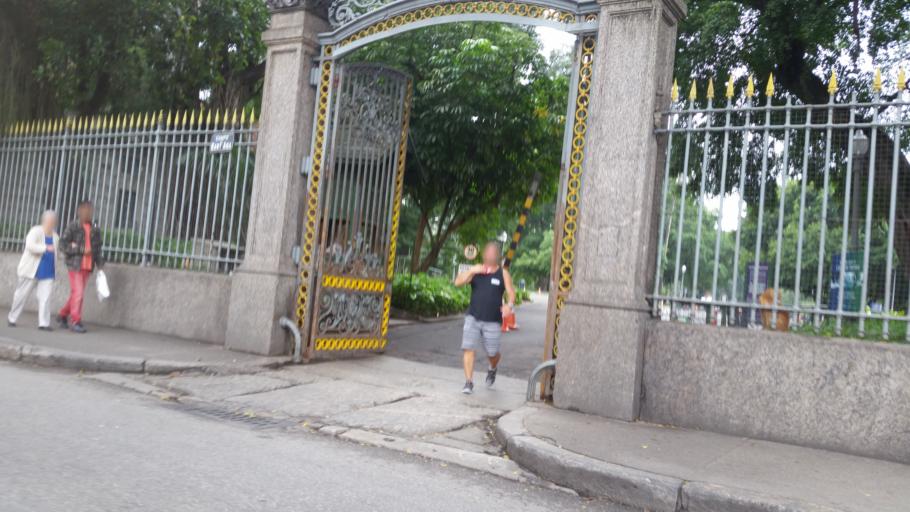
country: BR
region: Rio de Janeiro
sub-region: Rio De Janeiro
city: Rio de Janeiro
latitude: -22.9073
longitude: -43.1902
